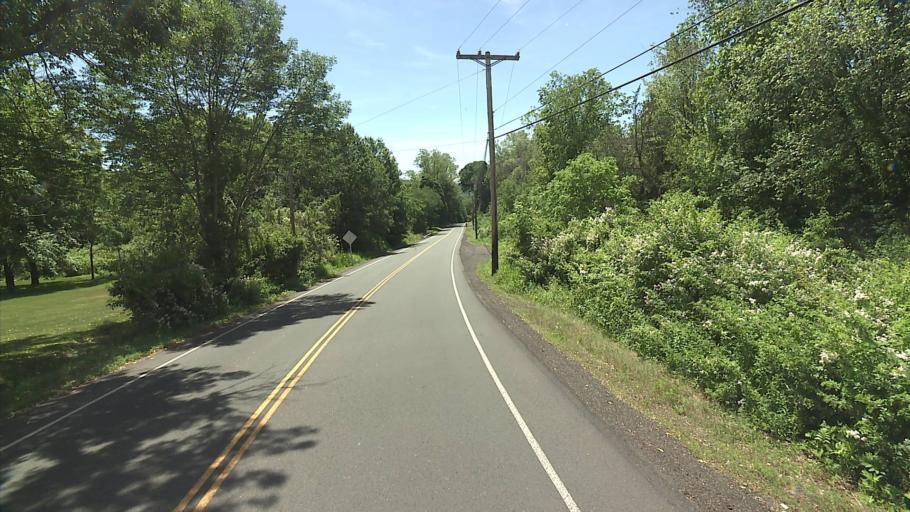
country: US
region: Connecticut
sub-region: New Haven County
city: Meriden
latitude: 41.5963
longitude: -72.8427
